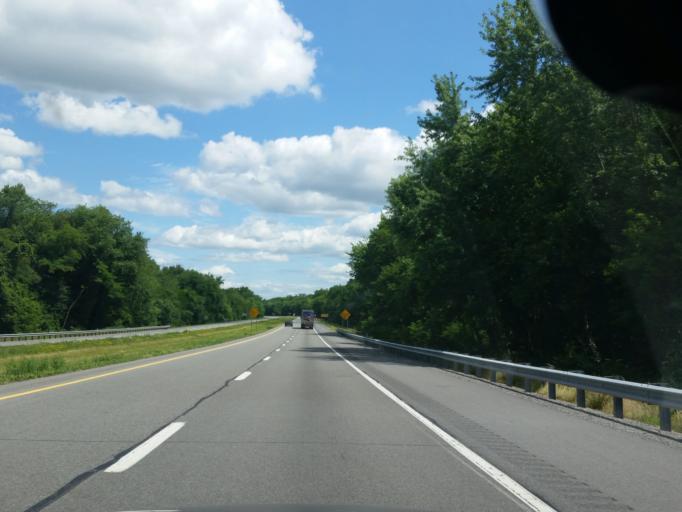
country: US
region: Pennsylvania
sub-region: Snyder County
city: Selinsgrove
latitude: 40.8049
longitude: -76.8540
